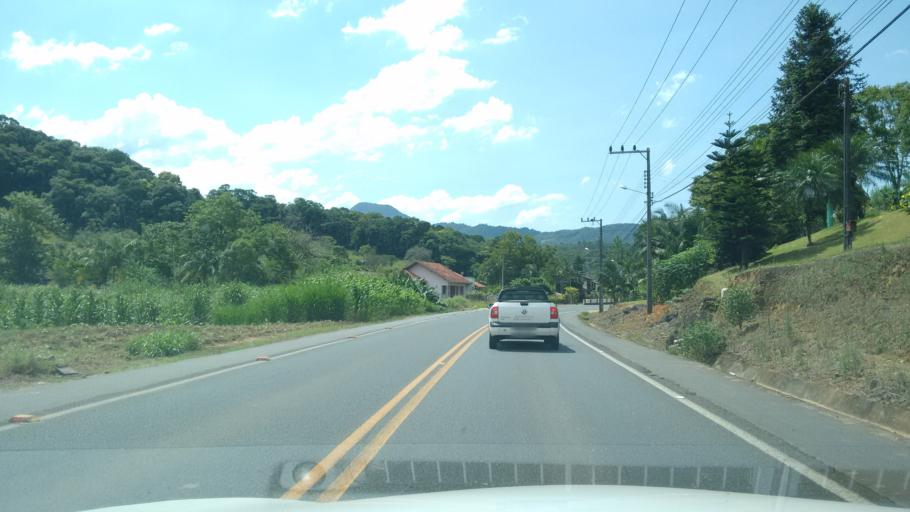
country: BR
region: Santa Catarina
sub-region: Pomerode
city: Pomerode
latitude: -26.7308
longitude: -49.2136
